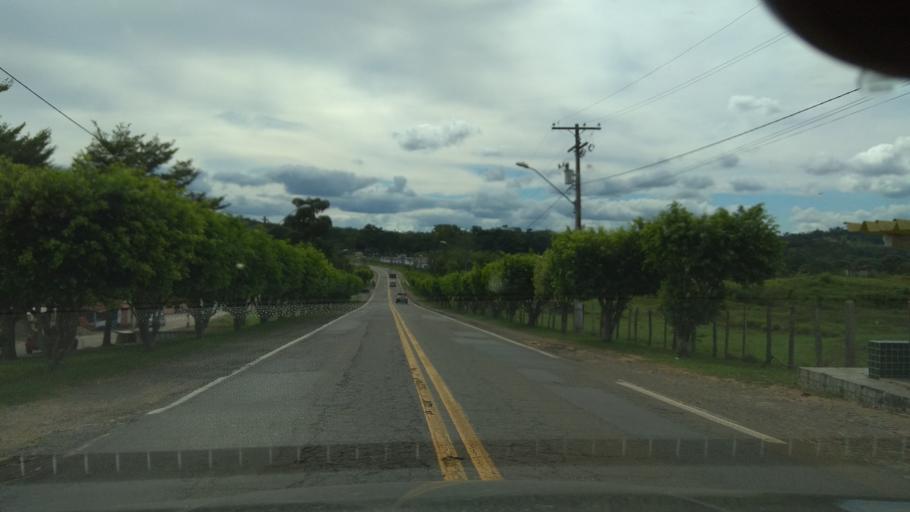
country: BR
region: Bahia
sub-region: Ubata
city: Ubata
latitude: -14.2048
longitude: -39.6044
